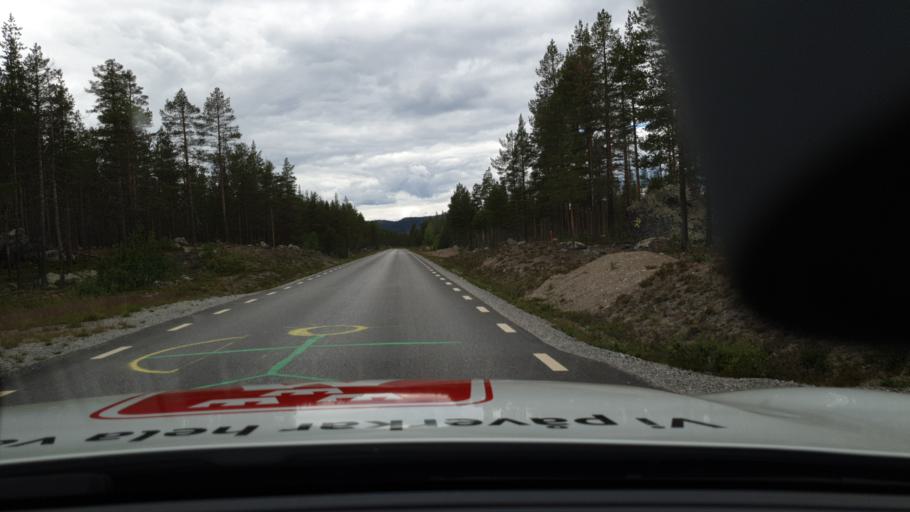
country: SE
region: Norrbotten
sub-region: Jokkmokks Kommun
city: Jokkmokk
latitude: 66.8688
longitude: 18.7749
